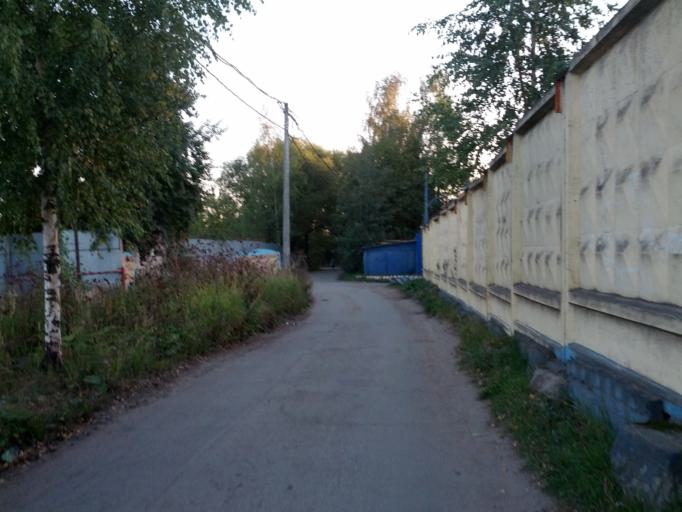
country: RU
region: St.-Petersburg
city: Obukhovo
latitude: 59.9102
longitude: 30.4353
